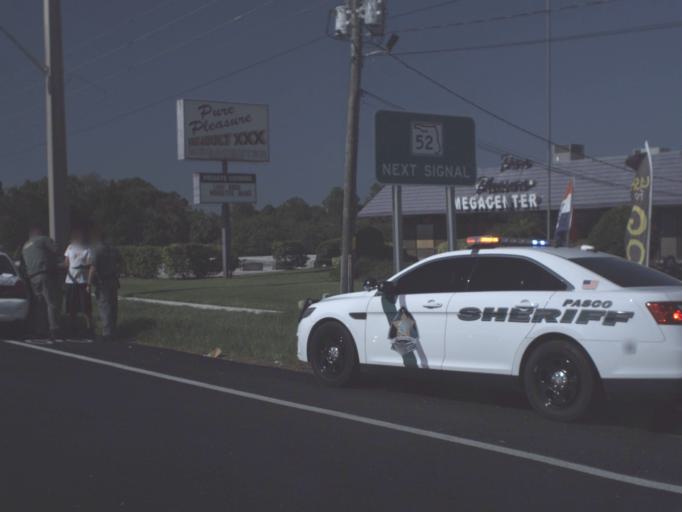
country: US
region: Florida
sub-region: Pasco County
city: Bayonet Point
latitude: 28.3381
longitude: -82.6994
